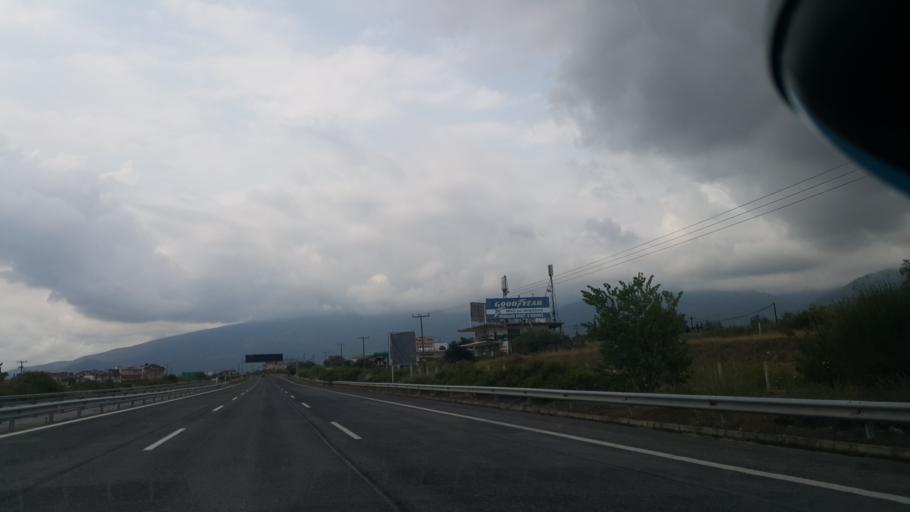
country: GR
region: Central Macedonia
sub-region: Nomos Pierias
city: Leptokarya
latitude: 40.0612
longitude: 22.5558
